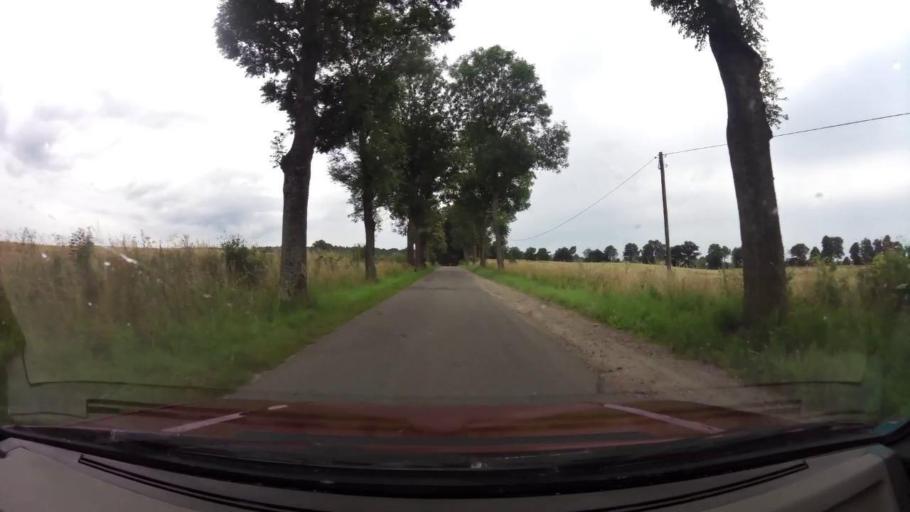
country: PL
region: West Pomeranian Voivodeship
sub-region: Powiat bialogardzki
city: Bialogard
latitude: 53.9520
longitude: 15.9648
